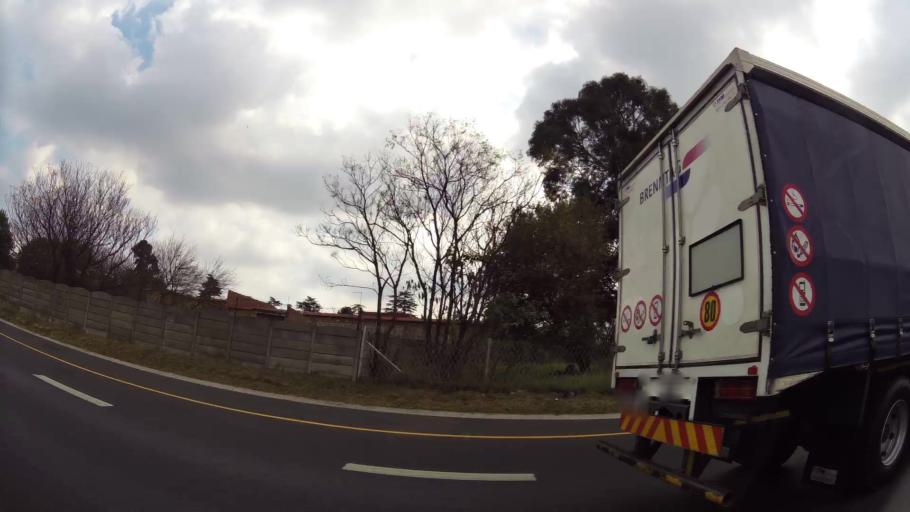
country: ZA
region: Gauteng
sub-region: Ekurhuleni Metropolitan Municipality
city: Benoni
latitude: -26.1776
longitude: 28.3260
